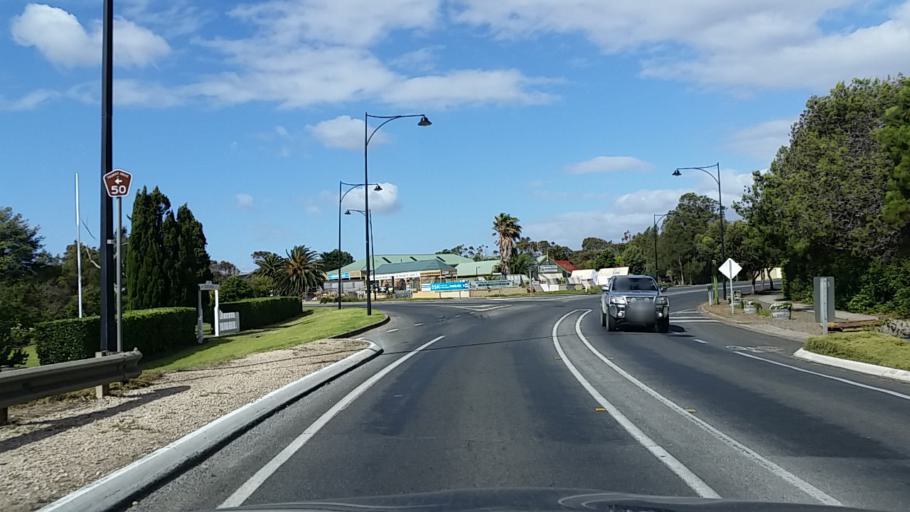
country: AU
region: South Australia
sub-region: Alexandrina
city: Port Elliot
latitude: -35.5078
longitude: 138.7088
